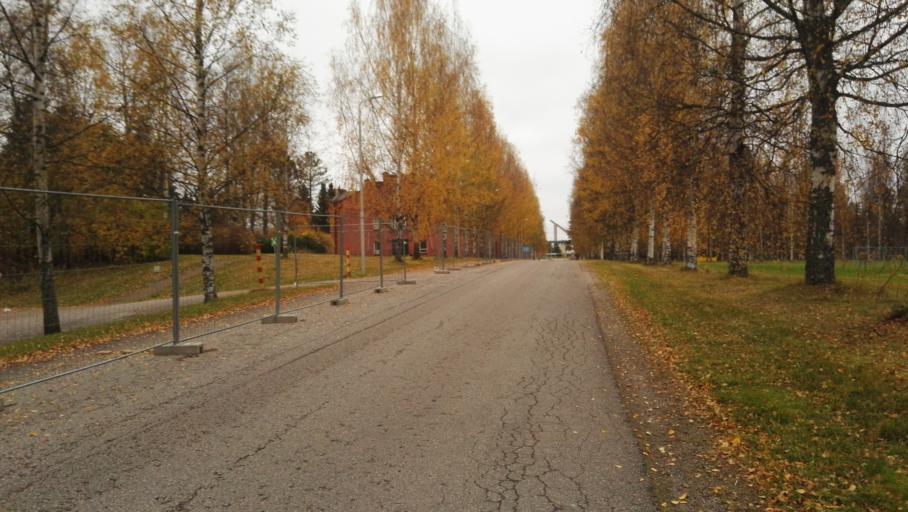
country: FI
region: Paijanne Tavastia
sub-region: Lahti
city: Lahti
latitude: 60.9670
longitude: 25.6235
